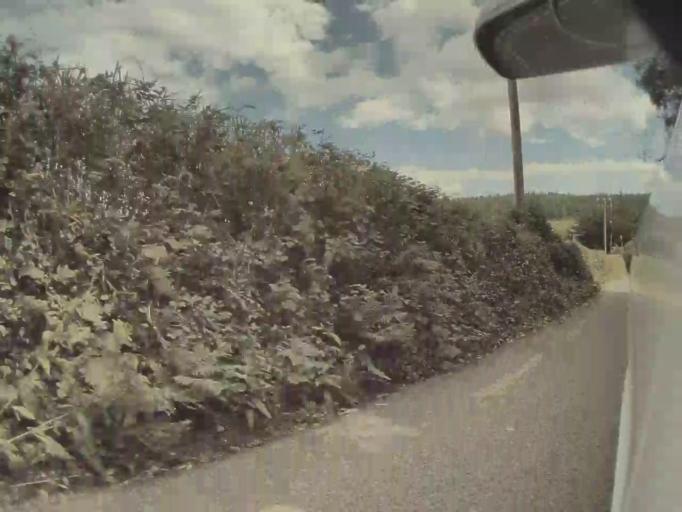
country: IE
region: Leinster
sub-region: Wicklow
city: Kilmacanoge
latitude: 53.1433
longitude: -6.1297
